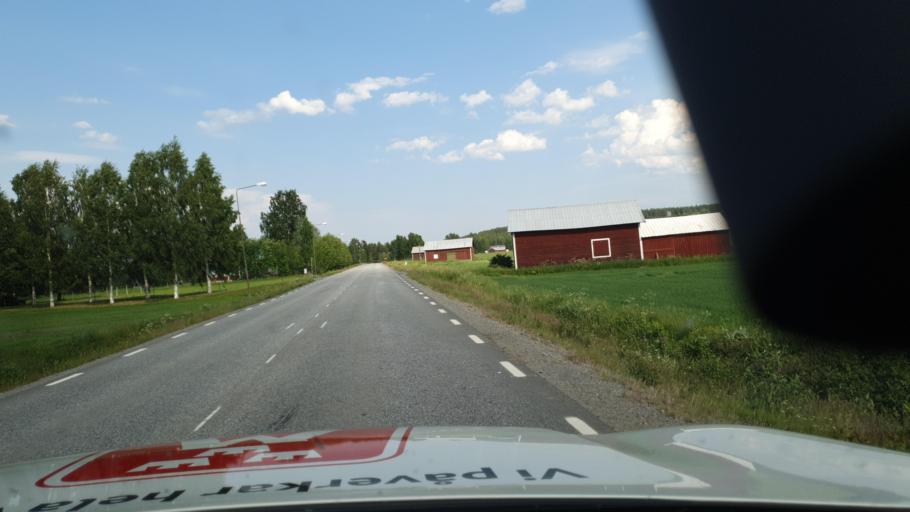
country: SE
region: Vaesterbotten
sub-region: Skelleftea Kommun
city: Viken
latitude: 64.7447
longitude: 20.8381
